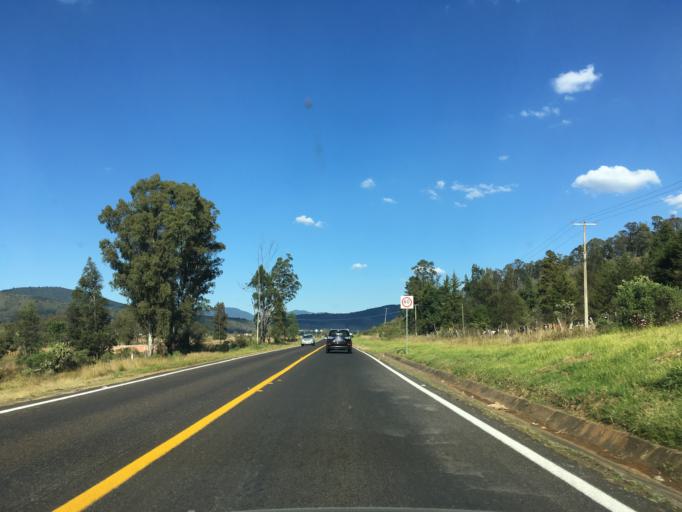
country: MX
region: Michoacan
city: Patzcuaro
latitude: 19.5637
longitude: -101.5778
